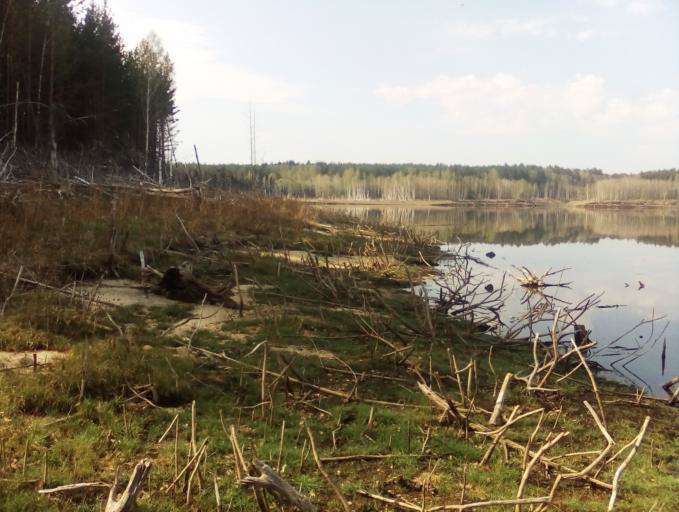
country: RU
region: Chelyabinsk
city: Nizhniy Ufaley
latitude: 55.7551
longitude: 60.1272
